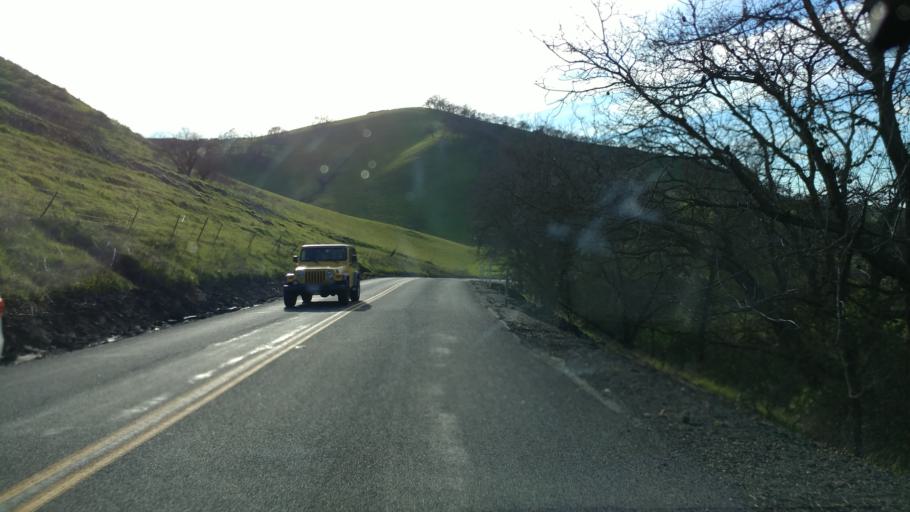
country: US
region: California
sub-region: Contra Costa County
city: Blackhawk
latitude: 37.7754
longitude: -121.8268
